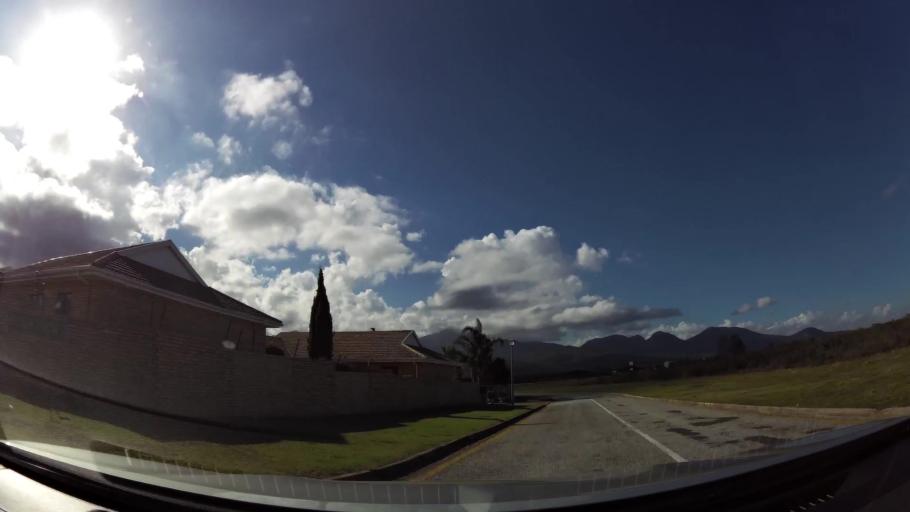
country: ZA
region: Western Cape
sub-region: Eden District Municipality
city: George
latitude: -33.9658
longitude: 22.4963
